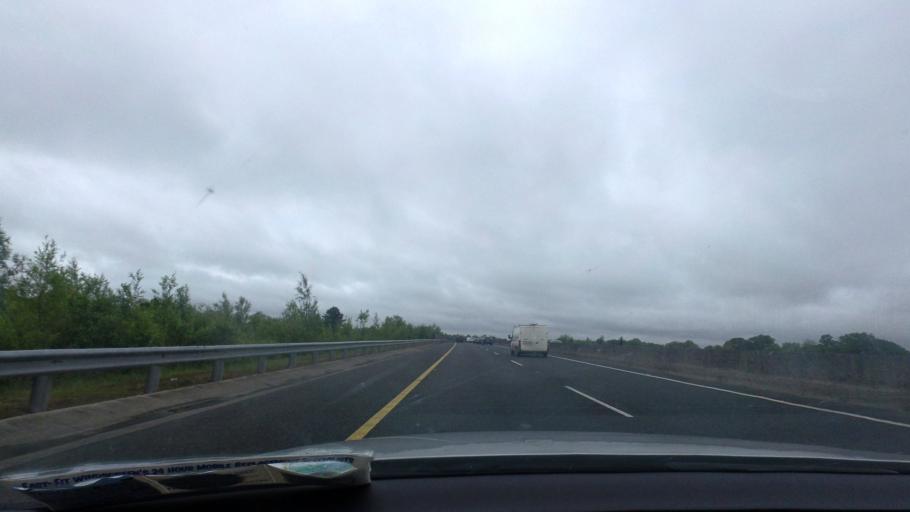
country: IE
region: Munster
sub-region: County Limerick
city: Castleconnell
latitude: 52.7074
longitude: -8.4822
